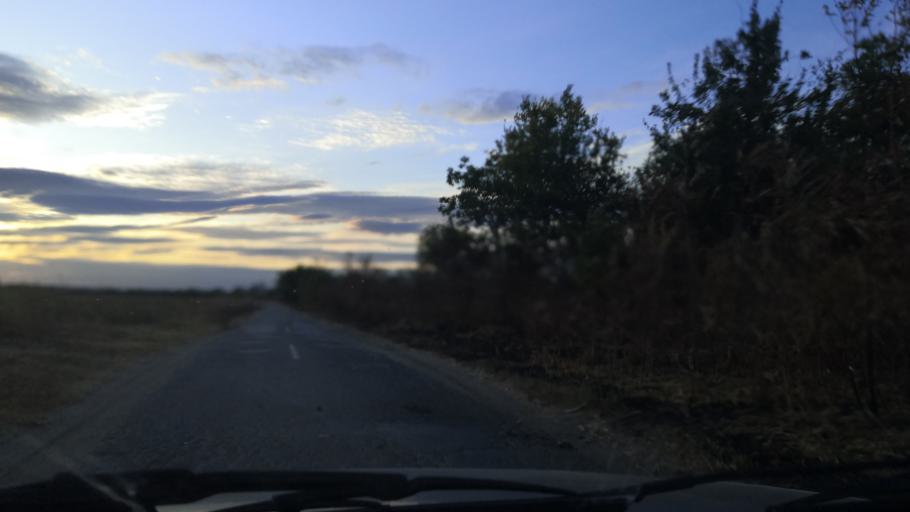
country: RO
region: Mehedinti
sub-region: Comuna Gruia
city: Izvoarele
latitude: 44.2782
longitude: 22.6537
